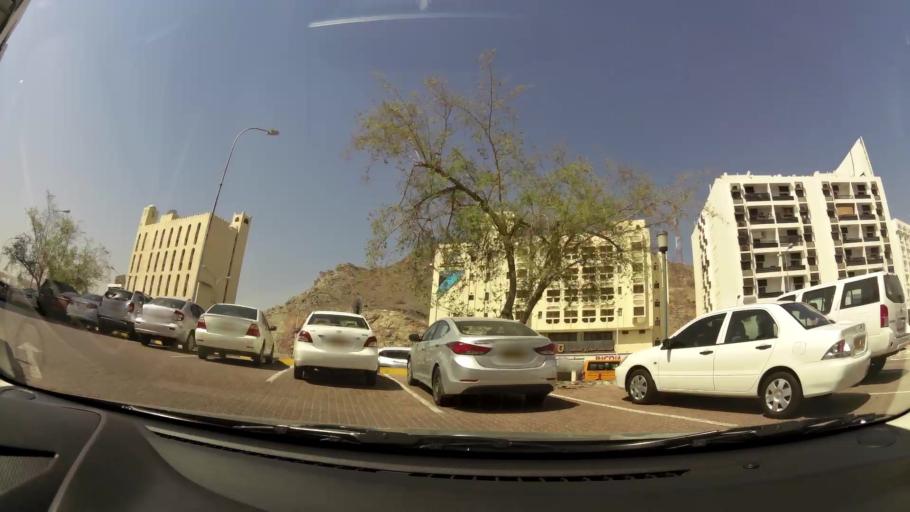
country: OM
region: Muhafazat Masqat
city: Muscat
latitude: 23.5960
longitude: 58.5415
